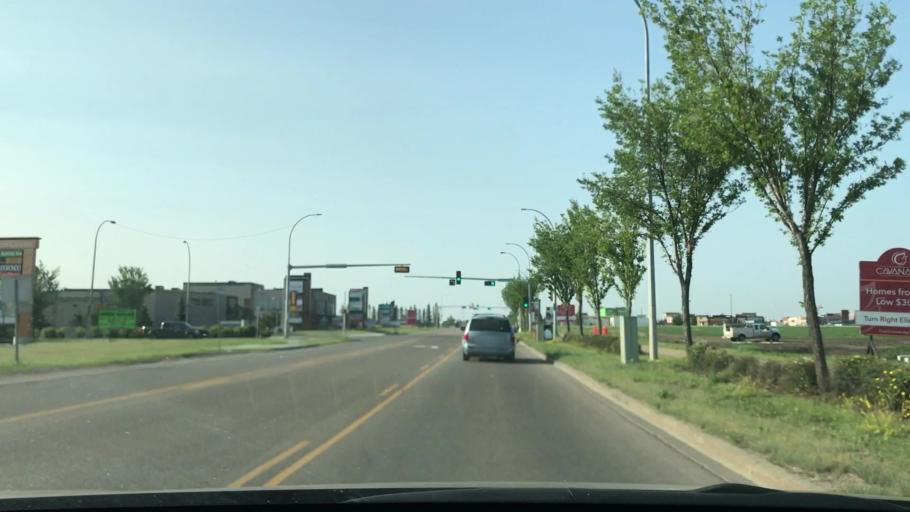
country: CA
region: Alberta
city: Beaumont
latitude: 53.4302
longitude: -113.4800
